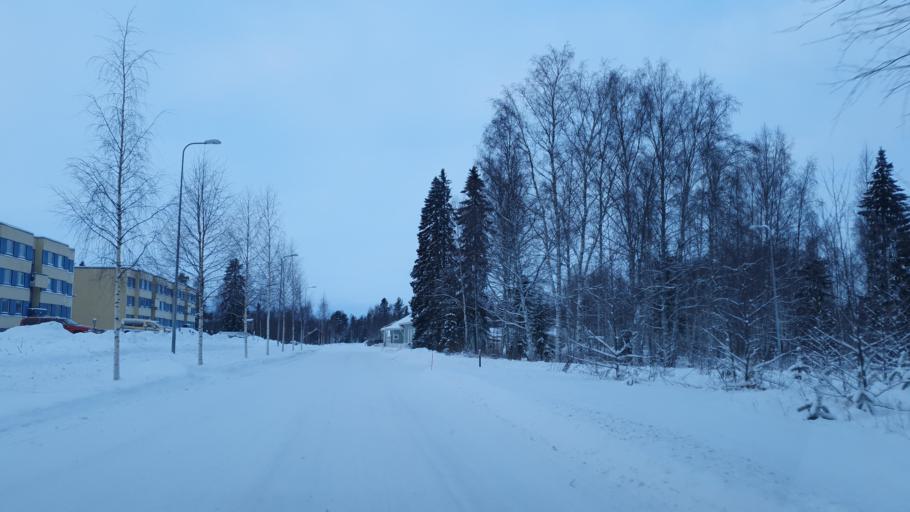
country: FI
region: Northern Ostrobothnia
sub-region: Oulu
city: Haukipudas
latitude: 65.2132
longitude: 25.3070
